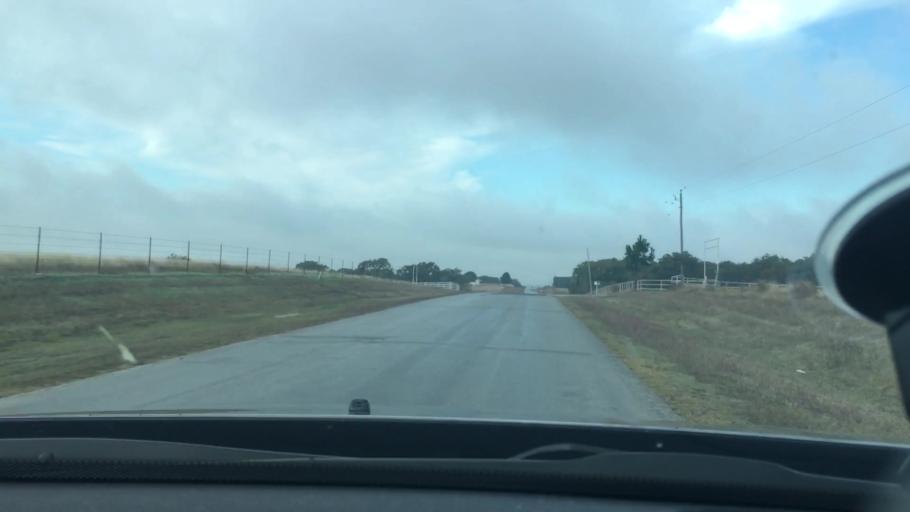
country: US
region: Oklahoma
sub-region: Murray County
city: Sulphur
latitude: 34.6223
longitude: -96.9503
